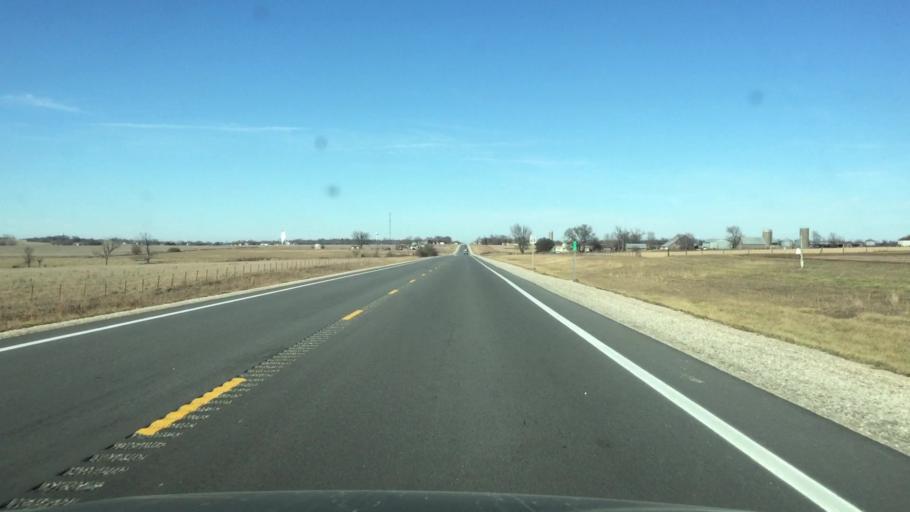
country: US
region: Kansas
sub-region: Anderson County
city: Garnett
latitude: 38.3713
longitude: -95.2486
